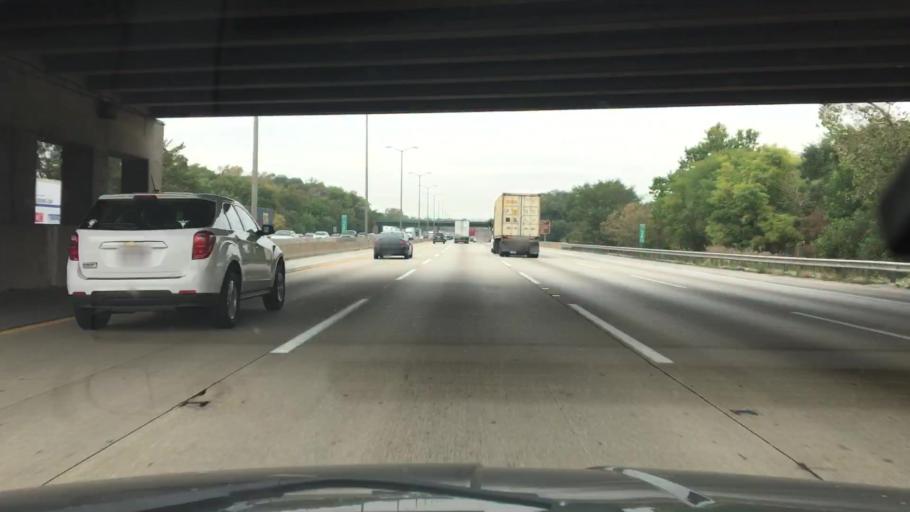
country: US
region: Illinois
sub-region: Cook County
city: Western Springs
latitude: 41.8042
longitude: -87.9108
